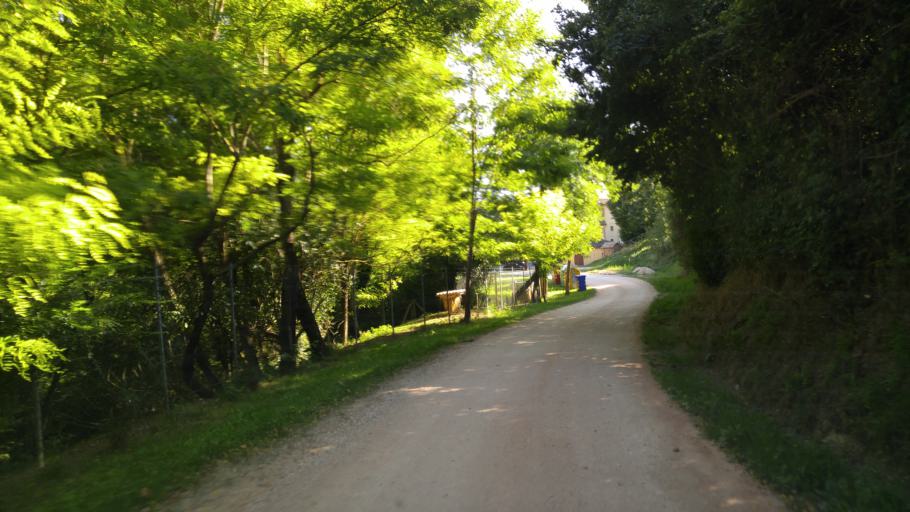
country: IT
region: The Marches
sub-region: Provincia di Pesaro e Urbino
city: Peglio
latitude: 43.6897
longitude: 12.5158
